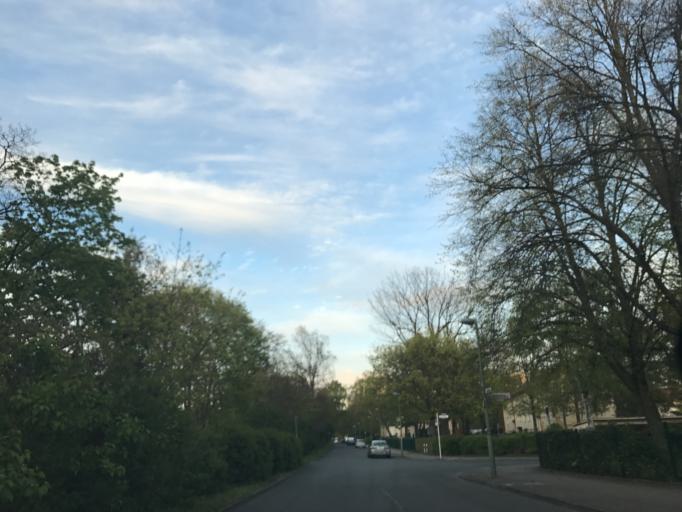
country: DE
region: Berlin
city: Haselhorst
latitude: 52.5099
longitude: 13.2360
